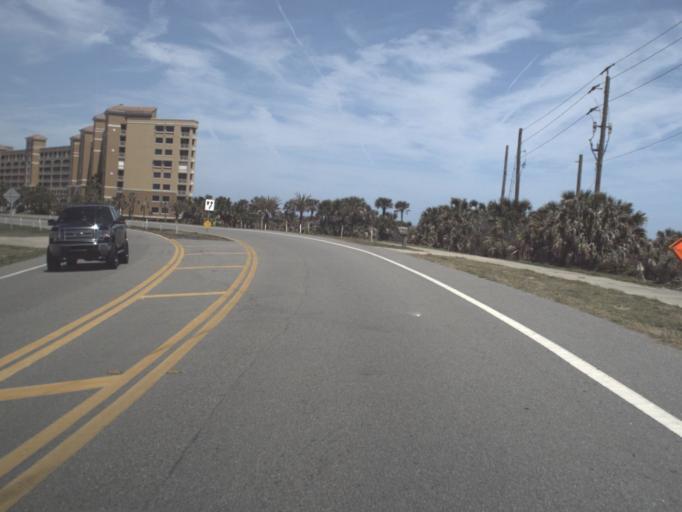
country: US
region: Florida
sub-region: Flagler County
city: Palm Coast
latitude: 29.6435
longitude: -81.2034
